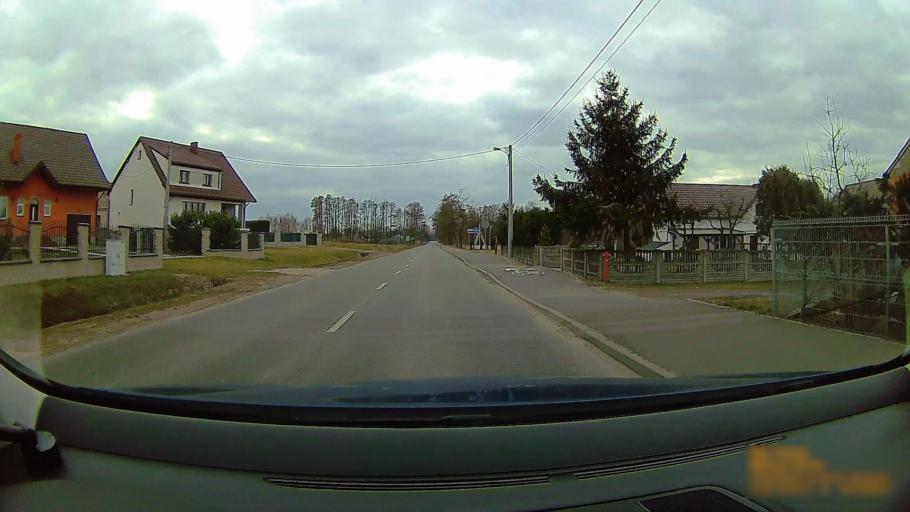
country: PL
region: Greater Poland Voivodeship
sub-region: Powiat koninski
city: Rzgow Pierwszy
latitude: 52.1755
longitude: 18.0938
